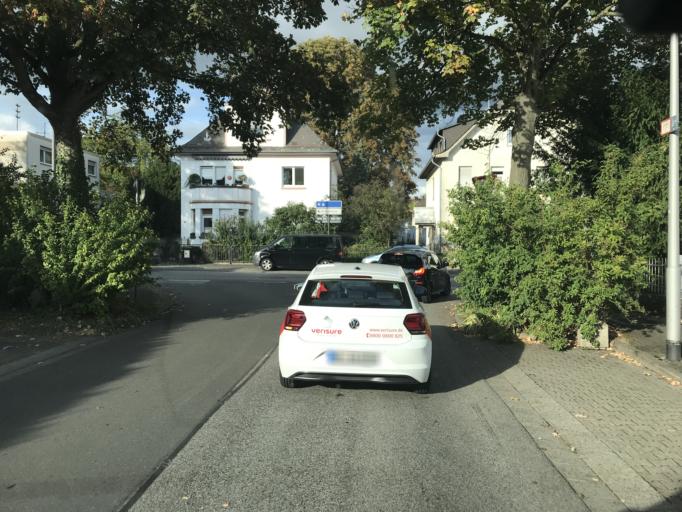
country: DE
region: Hesse
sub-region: Regierungsbezirk Darmstadt
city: Wiesbaden
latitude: 50.0575
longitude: 8.2917
